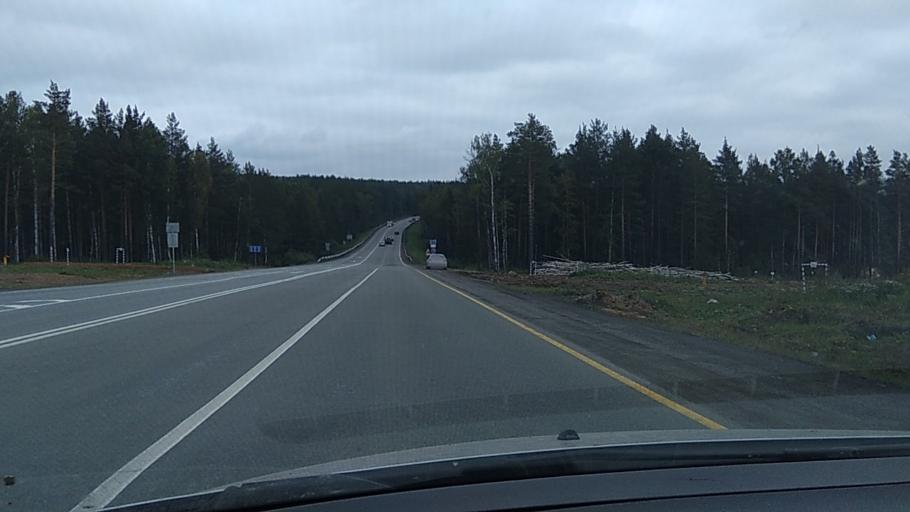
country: RU
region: Chelyabinsk
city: Zlatoust
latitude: 55.0556
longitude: 59.6974
